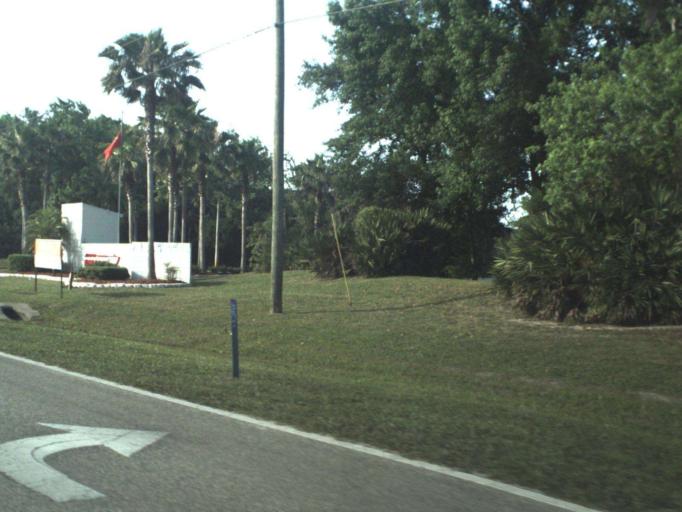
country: US
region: Florida
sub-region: Volusia County
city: Oak Hill
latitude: 28.9206
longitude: -80.8718
